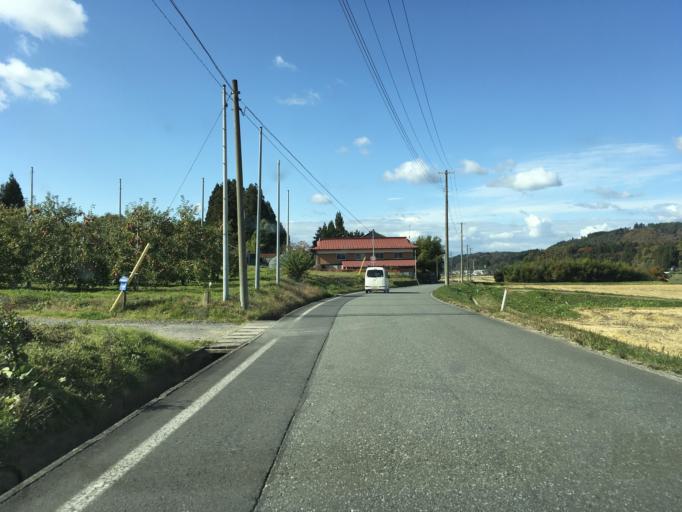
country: JP
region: Iwate
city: Ichinoseki
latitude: 38.9497
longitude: 141.3941
